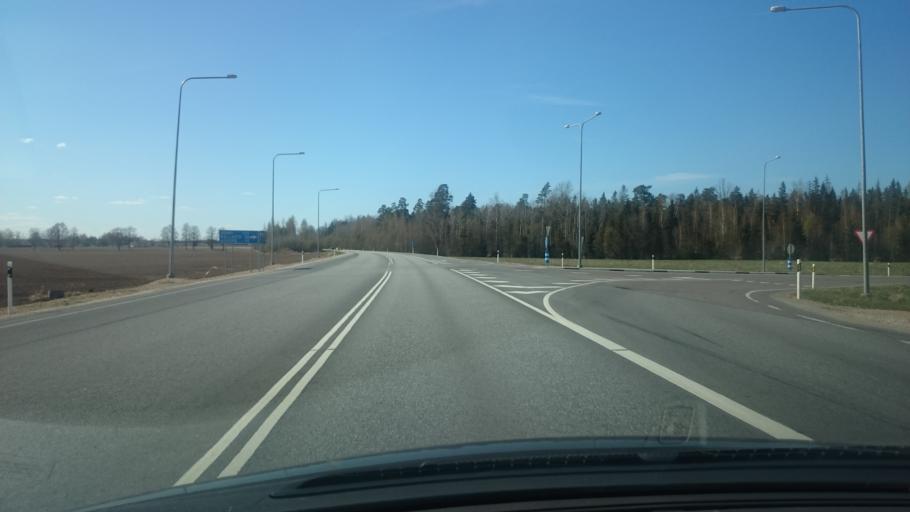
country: EE
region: Tartu
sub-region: Tartu linn
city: Tartu
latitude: 58.3675
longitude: 26.8839
